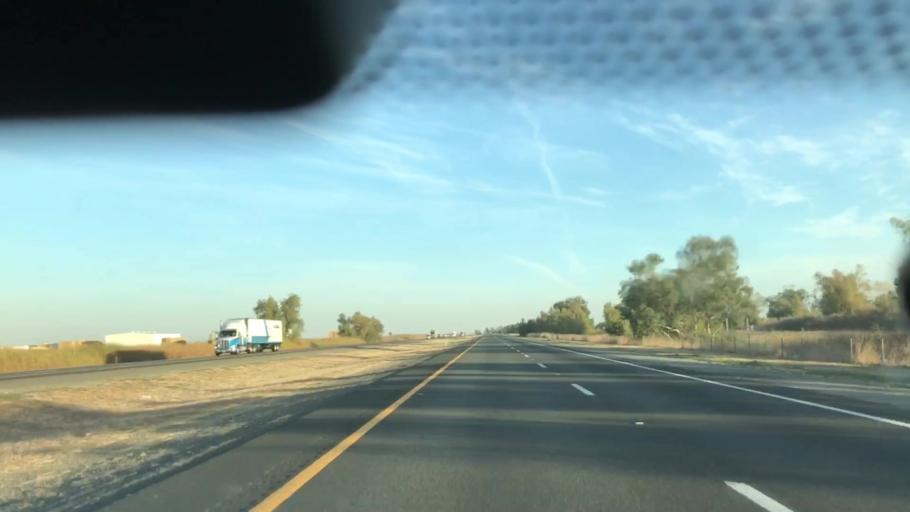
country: US
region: California
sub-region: Colusa County
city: Maxwell
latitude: 39.3814
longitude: -122.1929
